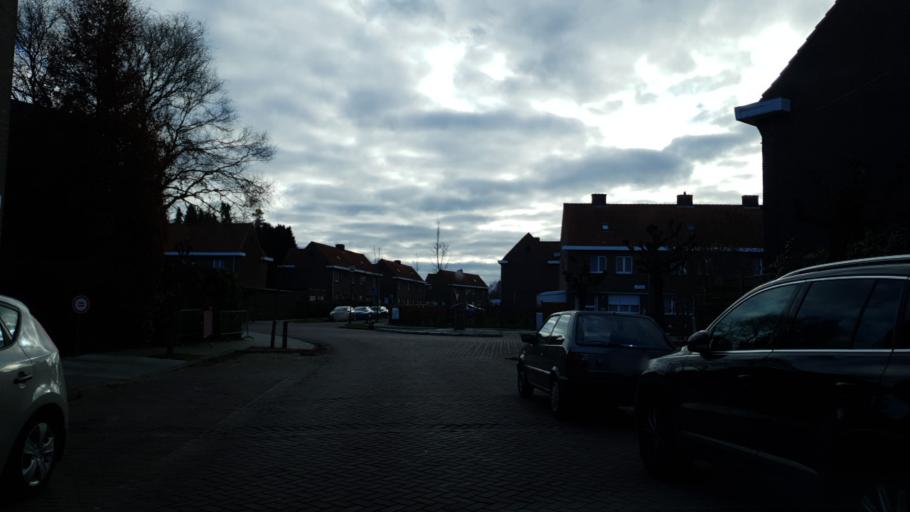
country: BE
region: Flanders
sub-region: Provincie Antwerpen
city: Lier
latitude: 51.1435
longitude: 4.5725
